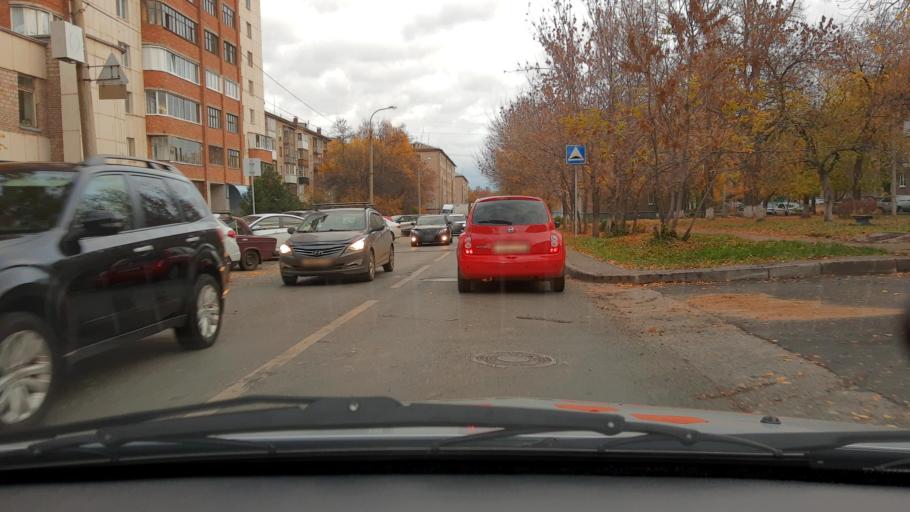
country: RU
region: Bashkortostan
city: Ufa
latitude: 54.7884
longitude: 56.0300
